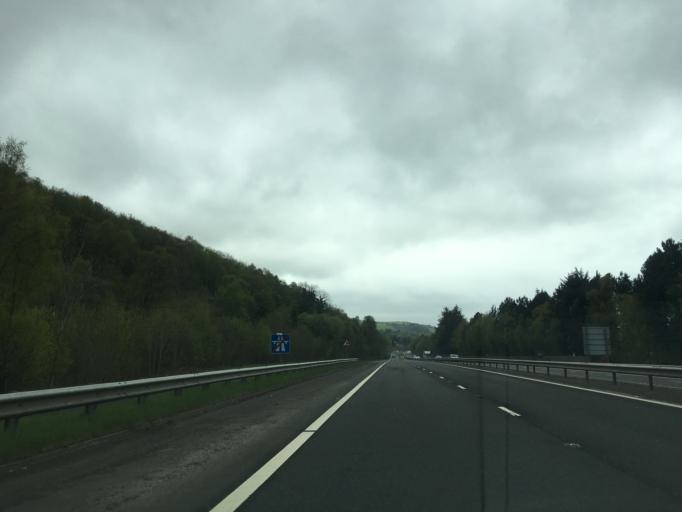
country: GB
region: Scotland
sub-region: West Dunbartonshire
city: Dumbarton
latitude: 55.9234
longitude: -4.5582
